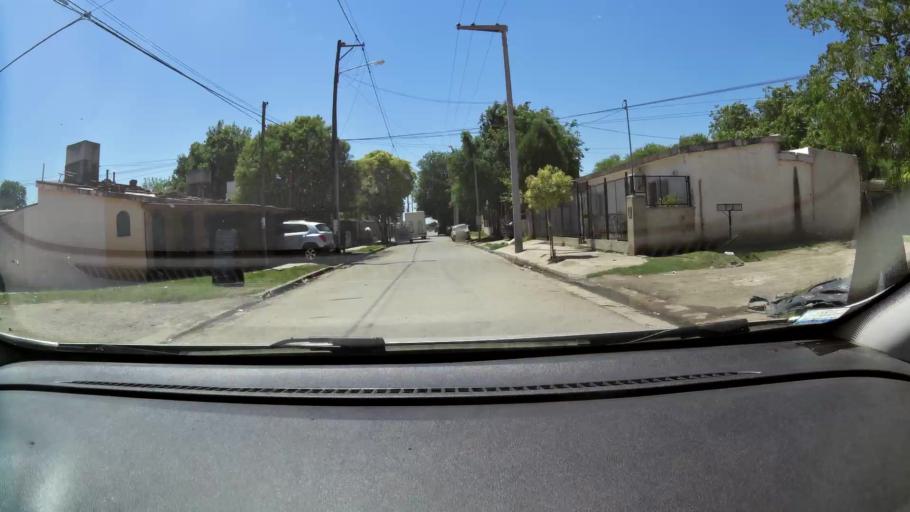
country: AR
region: Cordoba
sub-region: Departamento de Capital
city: Cordoba
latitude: -31.4376
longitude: -64.1217
